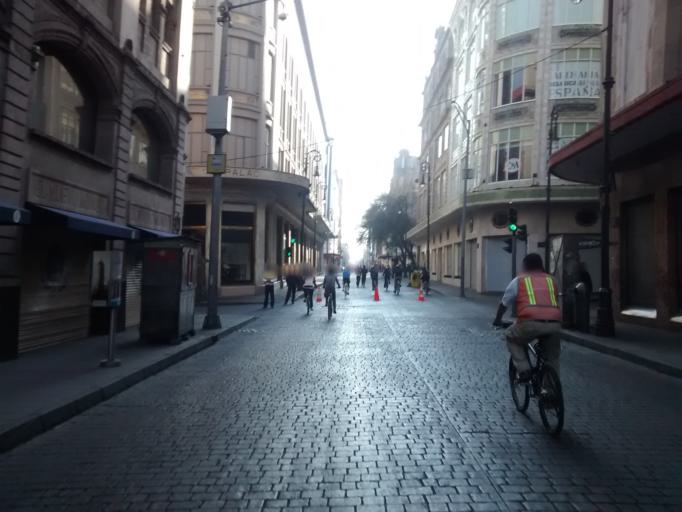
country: MX
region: Mexico City
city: Mexico City
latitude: 19.4312
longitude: -99.1348
